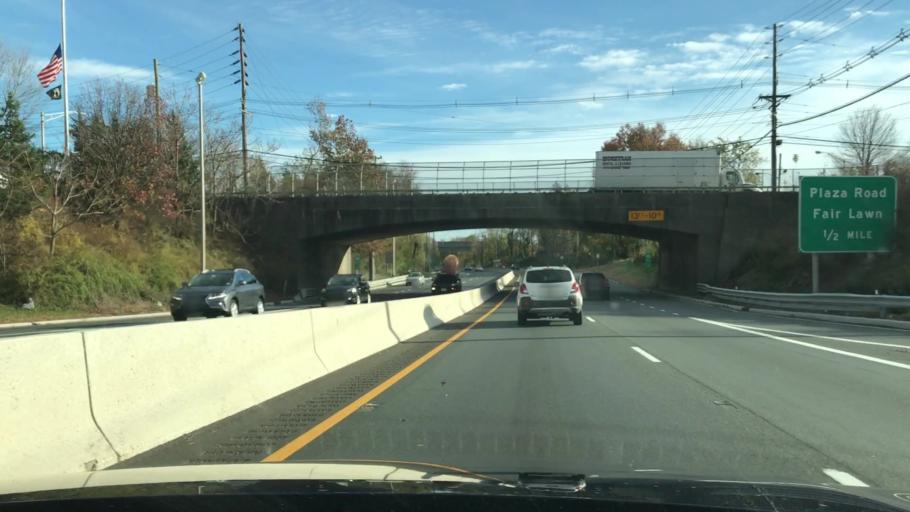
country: US
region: New Jersey
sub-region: Bergen County
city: Fair Lawn
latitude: 40.9383
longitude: -74.1260
